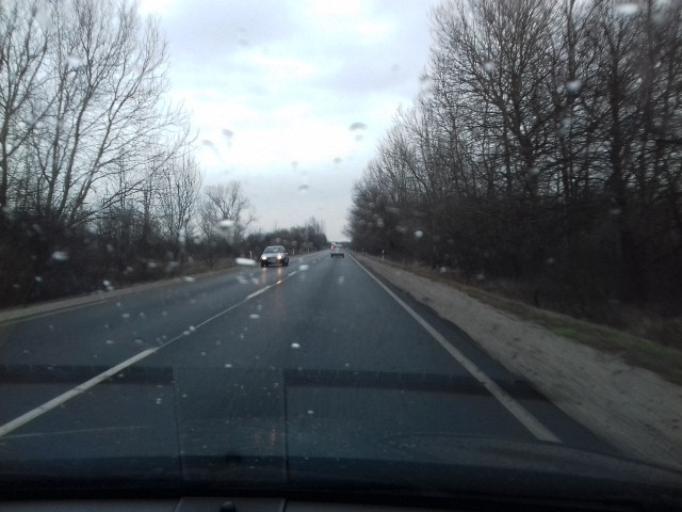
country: HU
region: Szabolcs-Szatmar-Bereg
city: Ujfeherto
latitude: 47.8437
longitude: 21.7045
